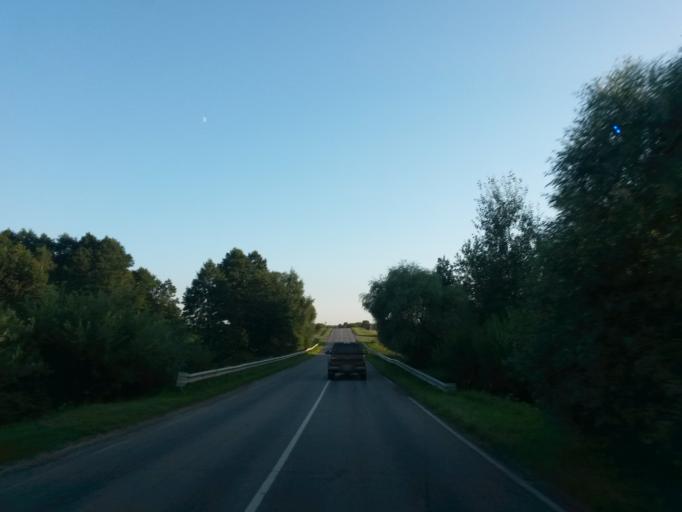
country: RU
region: Moskovskaya
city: Barybino
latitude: 55.2222
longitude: 37.7902
